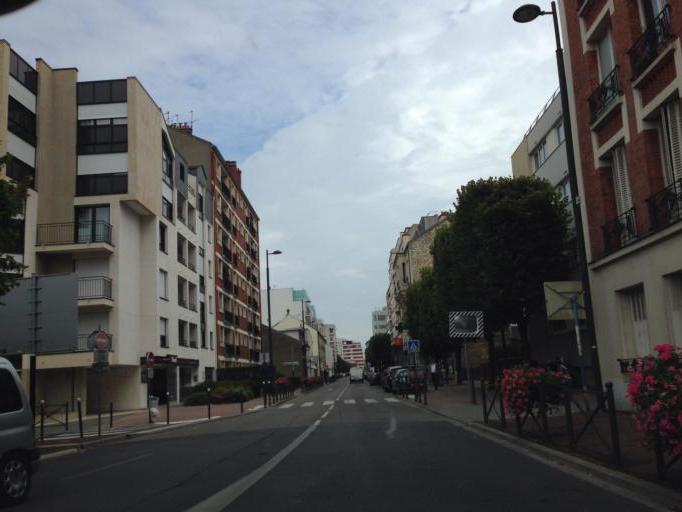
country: FR
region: Ile-de-France
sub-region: Departement des Hauts-de-Seine
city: Vanves
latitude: 48.8206
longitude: 2.2914
